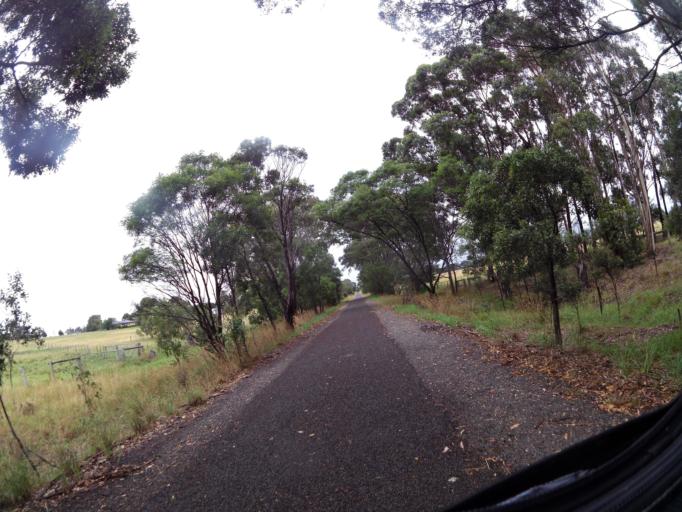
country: AU
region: Victoria
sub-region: East Gippsland
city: Bairnsdale
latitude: -37.8232
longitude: 147.7072
